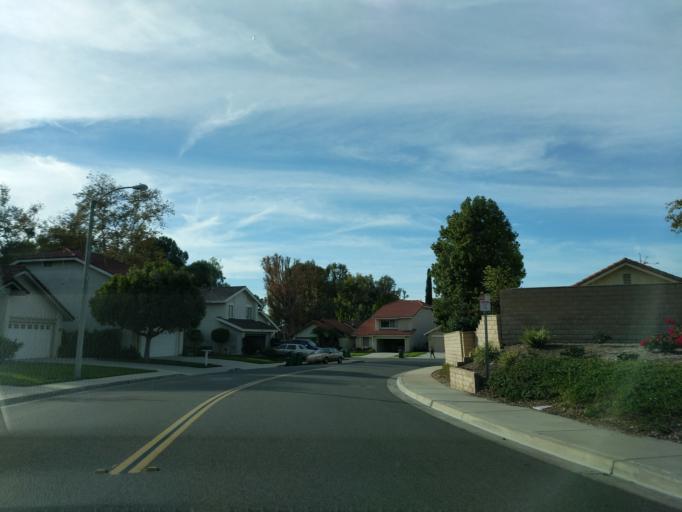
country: US
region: California
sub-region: Orange County
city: North Tustin
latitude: 33.7156
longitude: -117.7549
